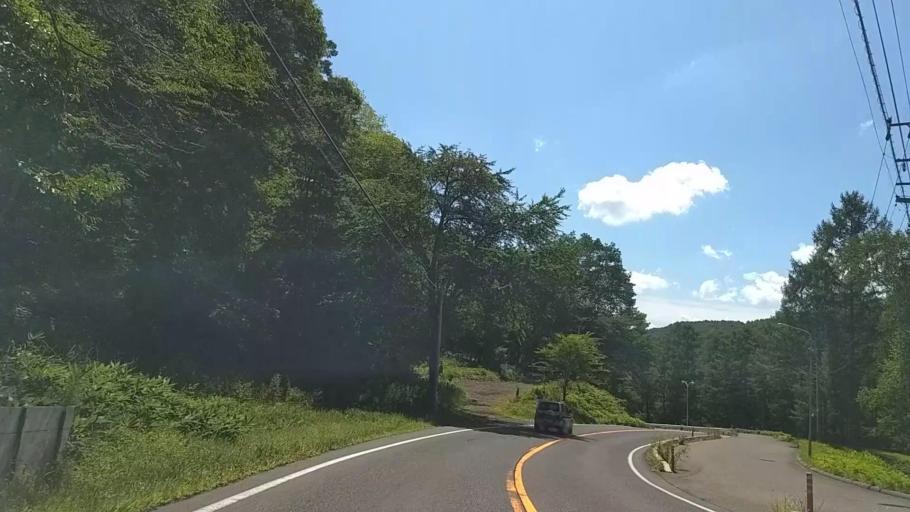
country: JP
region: Nagano
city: Chino
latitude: 36.0805
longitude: 138.2218
